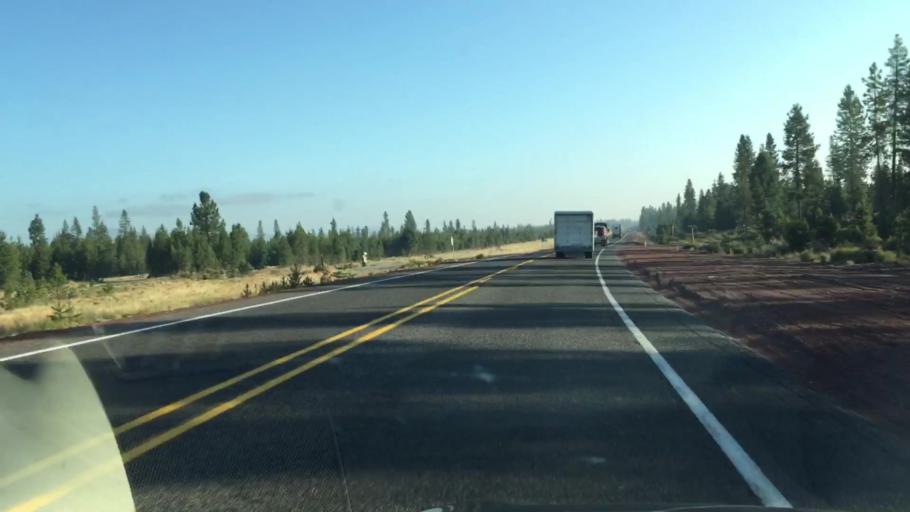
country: US
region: Oregon
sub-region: Deschutes County
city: La Pine
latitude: 43.4292
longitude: -121.7153
